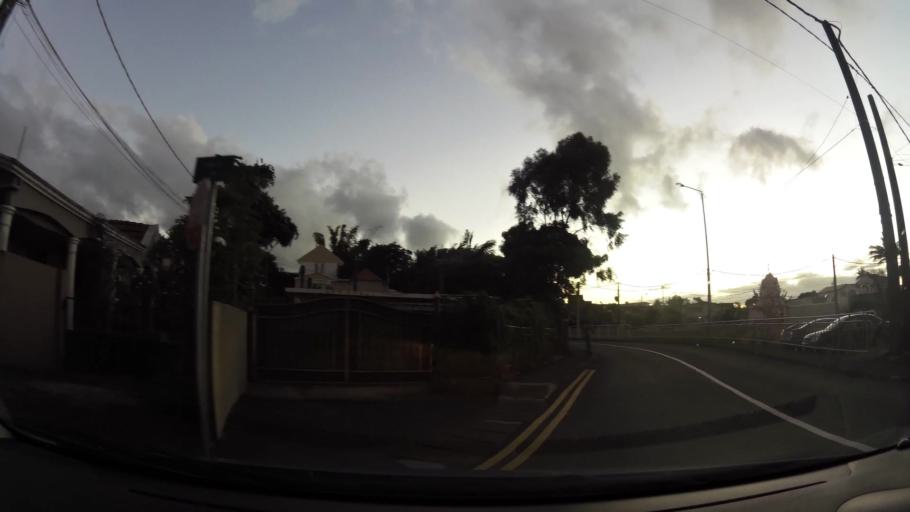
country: MU
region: Plaines Wilhems
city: Curepipe
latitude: -20.2932
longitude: 57.5197
